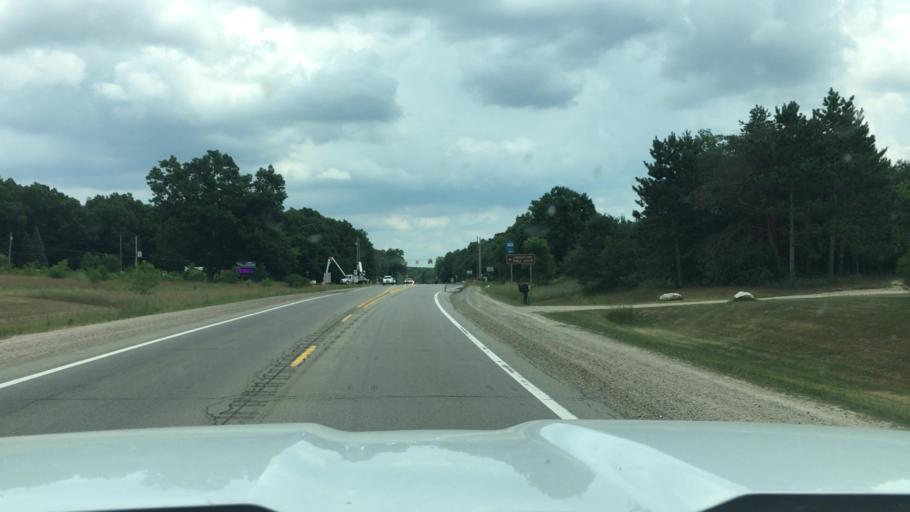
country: US
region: Michigan
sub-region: Montcalm County
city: Greenville
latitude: 43.1756
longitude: -85.3553
